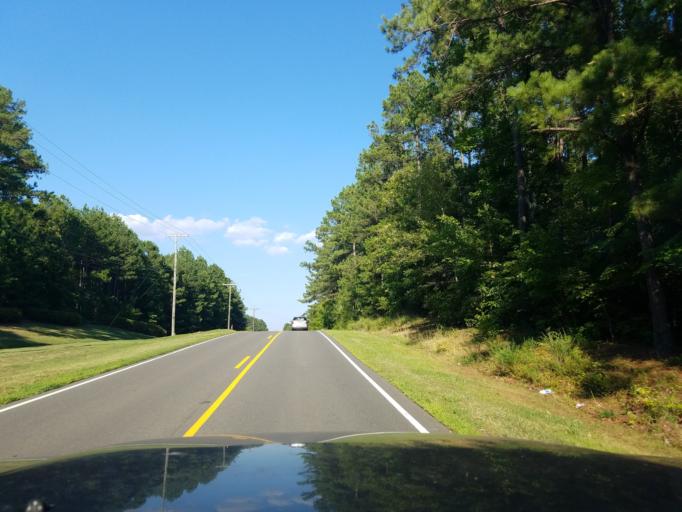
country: US
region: North Carolina
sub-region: Wake County
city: Green Level
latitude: 35.8754
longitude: -78.9233
